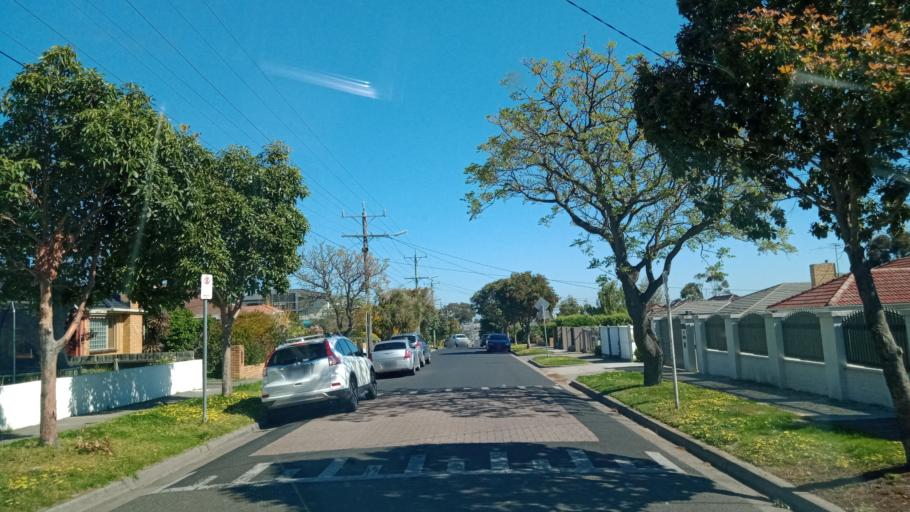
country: AU
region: Victoria
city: Highett
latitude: -37.9354
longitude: 145.0690
